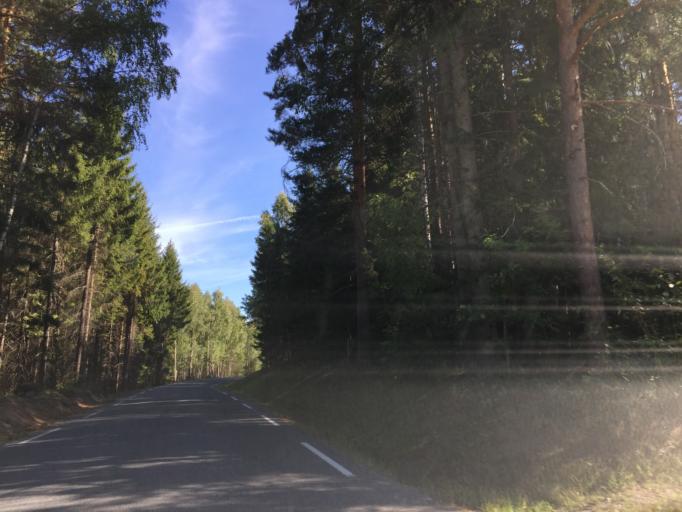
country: NO
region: Buskerud
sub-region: Ovre Eiker
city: Hokksund
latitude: 59.6941
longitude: 9.8423
